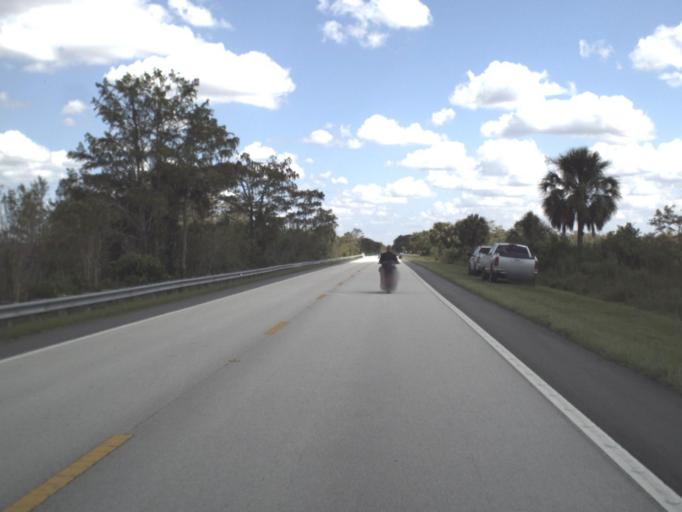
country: US
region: Florida
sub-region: Collier County
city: Marco
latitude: 25.8739
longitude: -81.2010
